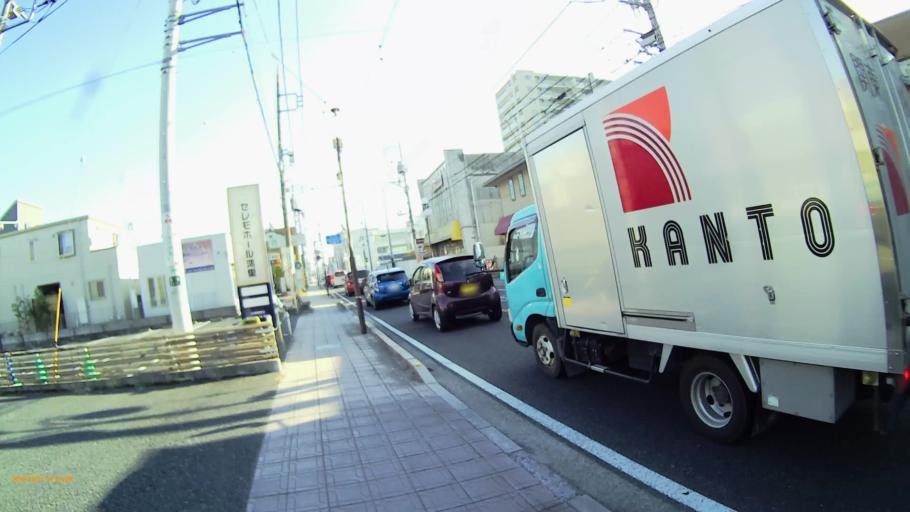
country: JP
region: Saitama
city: Konosu
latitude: 36.0611
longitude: 139.5117
